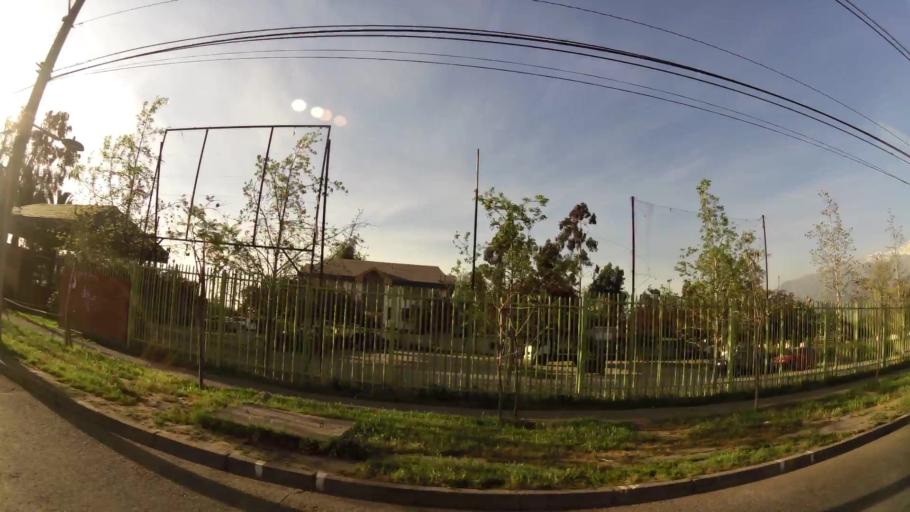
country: CL
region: Santiago Metropolitan
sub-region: Provincia de Cordillera
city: Puente Alto
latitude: -33.5436
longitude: -70.5783
